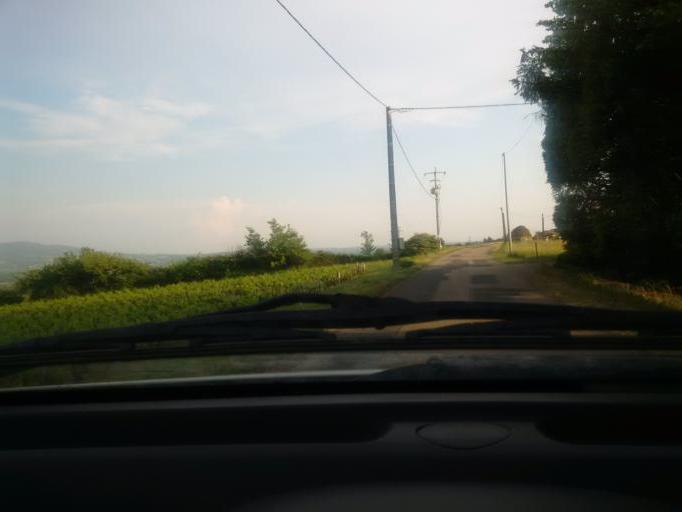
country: FR
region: Rhone-Alpes
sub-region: Departement du Rhone
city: Lucenay
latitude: 45.9201
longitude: 4.6987
